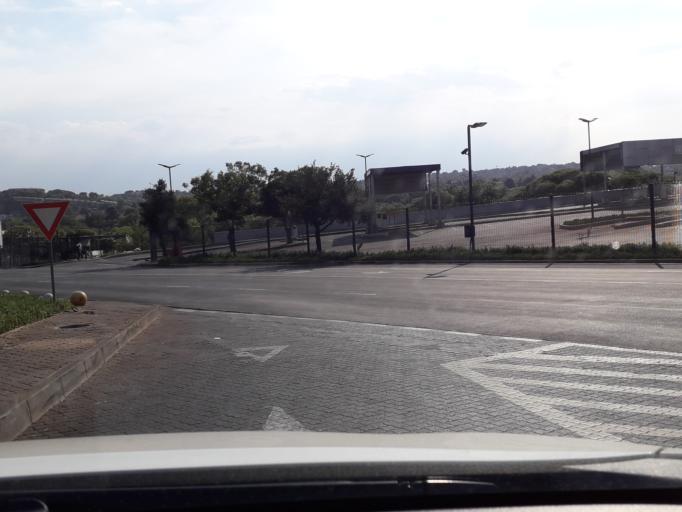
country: ZA
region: Gauteng
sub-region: City of Johannesburg Metropolitan Municipality
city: Johannesburg
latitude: -26.1288
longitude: 27.9713
